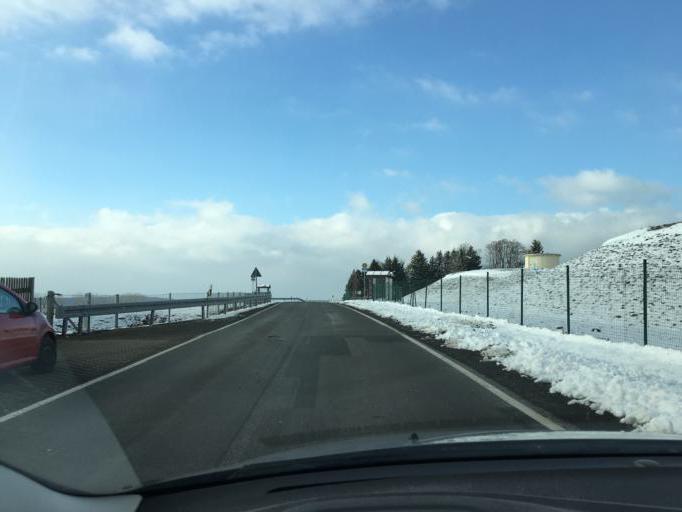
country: DE
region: Saxony
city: Grimma
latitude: 51.2493
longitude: 12.7055
